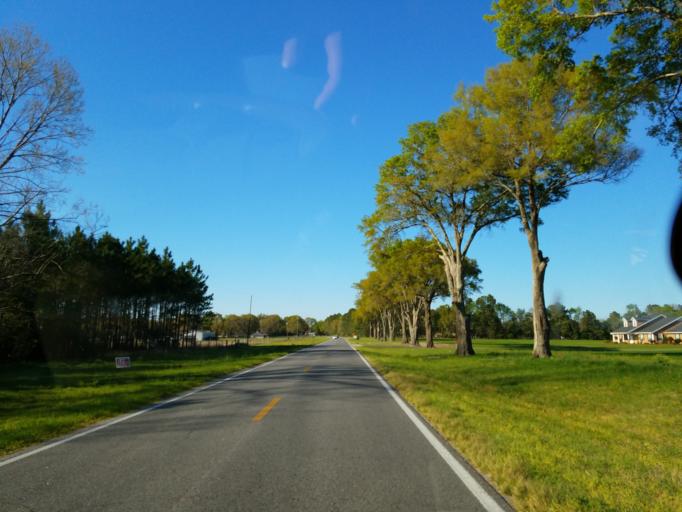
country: US
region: Florida
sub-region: Suwannee County
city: Wellborn
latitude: 30.0105
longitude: -82.8610
